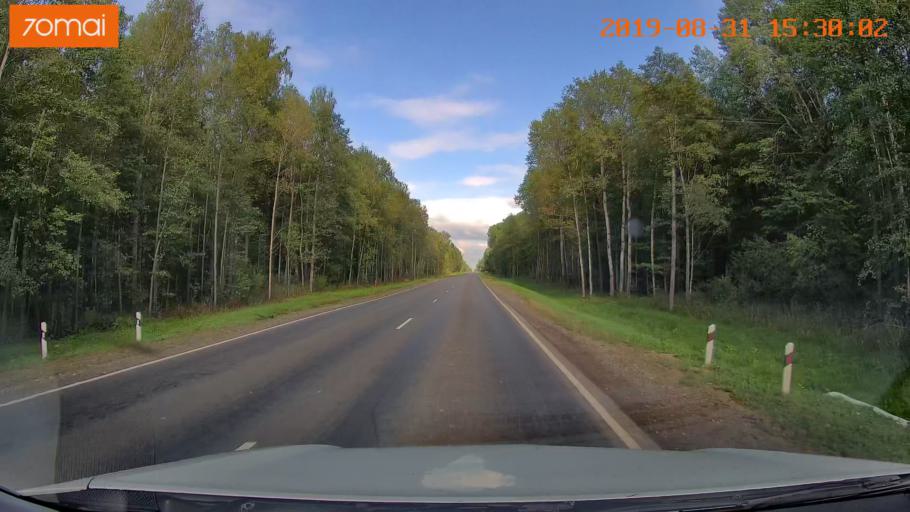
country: RU
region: Kaluga
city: Baryatino
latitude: 54.5729
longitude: 34.6200
